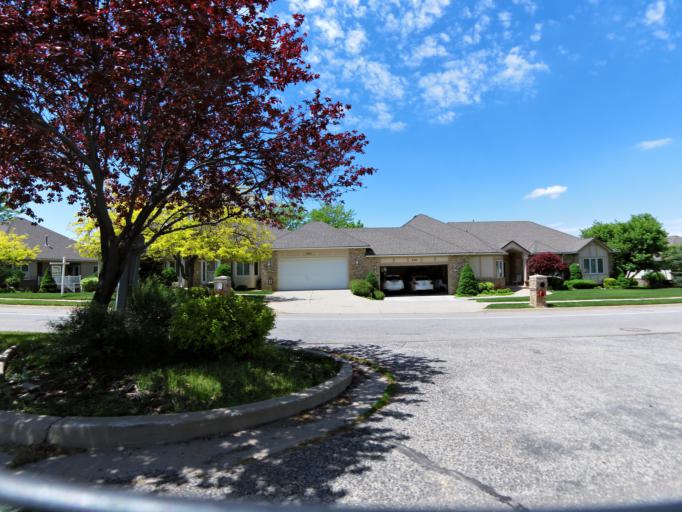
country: US
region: Utah
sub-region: Weber County
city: Uintah
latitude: 41.1768
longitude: -111.9321
